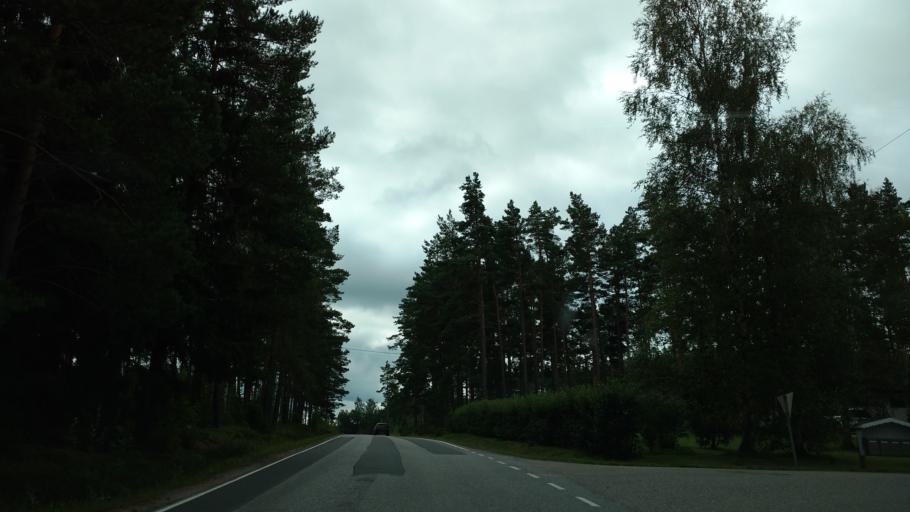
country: FI
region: Varsinais-Suomi
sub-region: Aboland-Turunmaa
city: Dragsfjaerd
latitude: 60.0683
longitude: 22.4503
